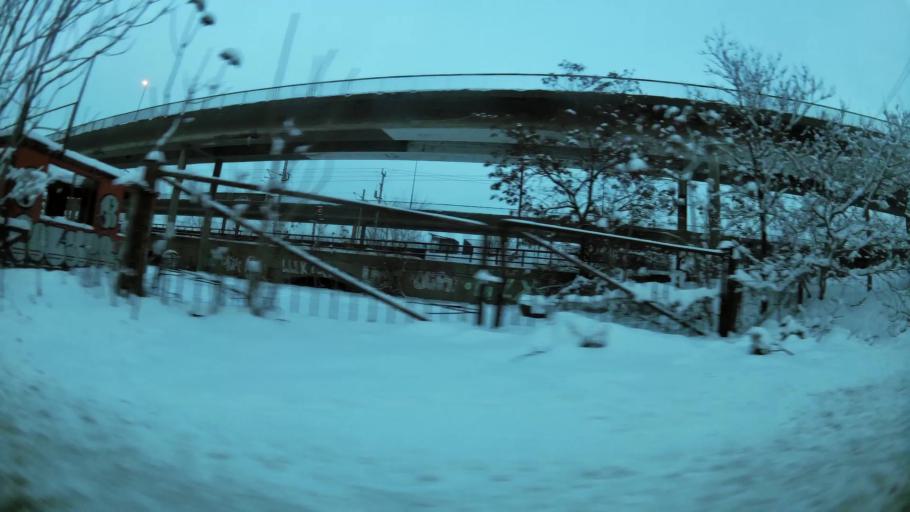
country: RS
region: Central Serbia
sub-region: Belgrade
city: Palilula
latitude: 44.8207
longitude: 20.4900
